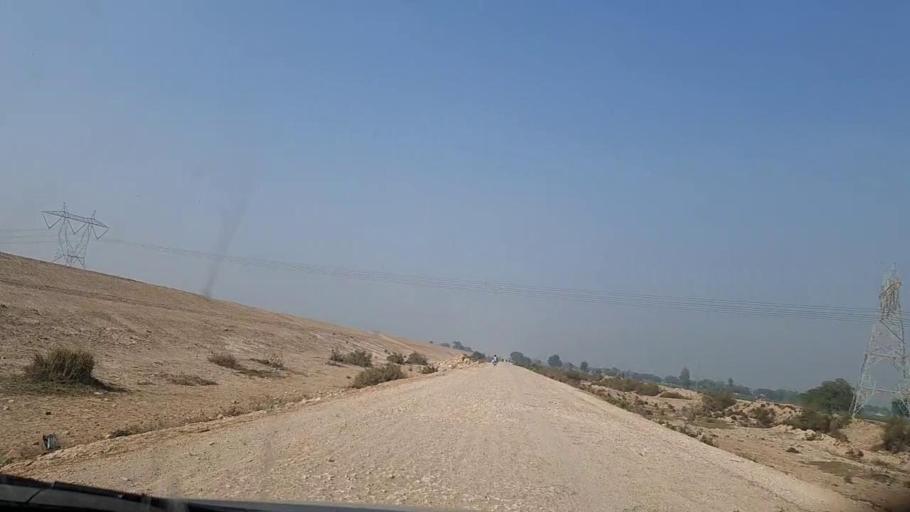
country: PK
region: Sindh
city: Moro
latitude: 26.7102
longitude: 67.9250
